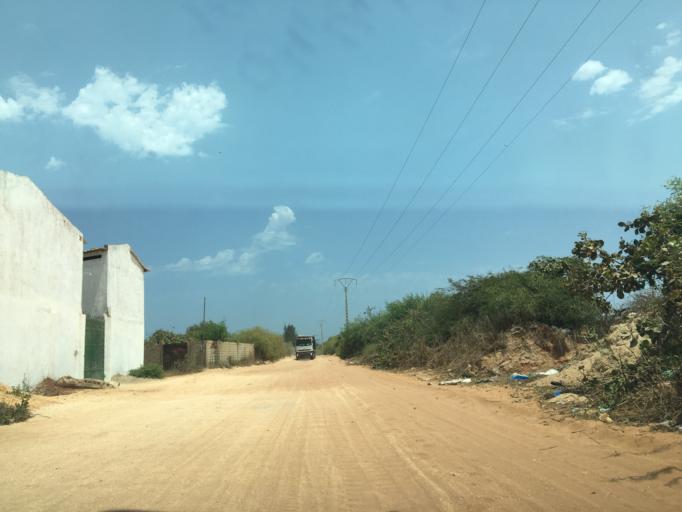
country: SN
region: Thies
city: Thies
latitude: 14.8127
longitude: -17.1925
